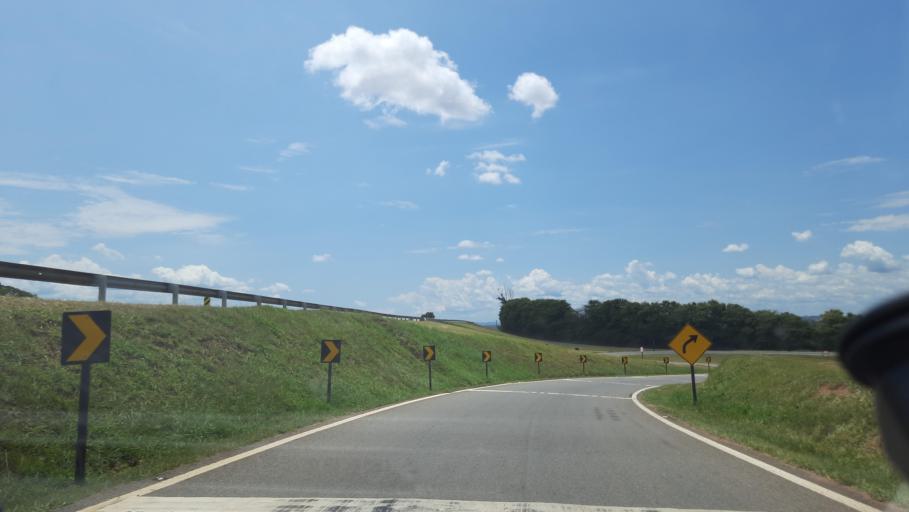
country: BR
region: Sao Paulo
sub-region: Mococa
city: Mococa
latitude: -21.5212
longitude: -47.0271
